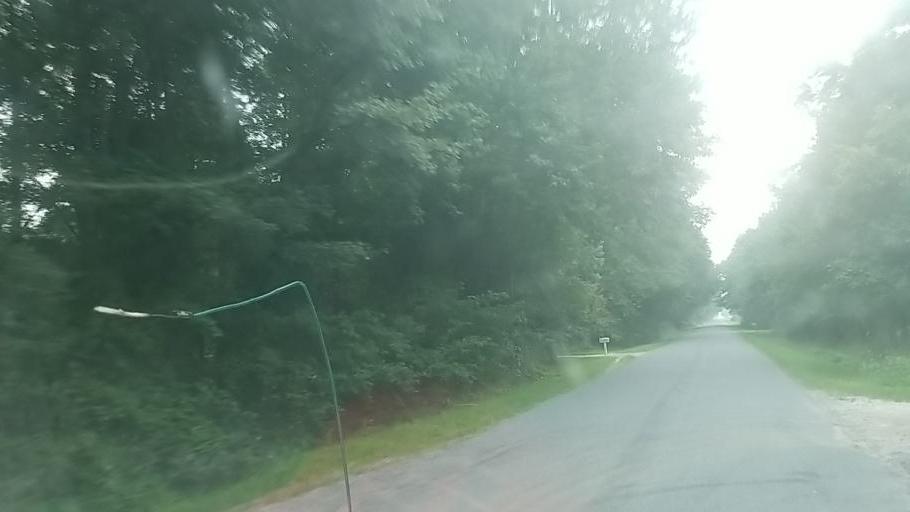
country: US
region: Maryland
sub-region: Wicomico County
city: Pittsville
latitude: 38.4521
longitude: -75.3813
